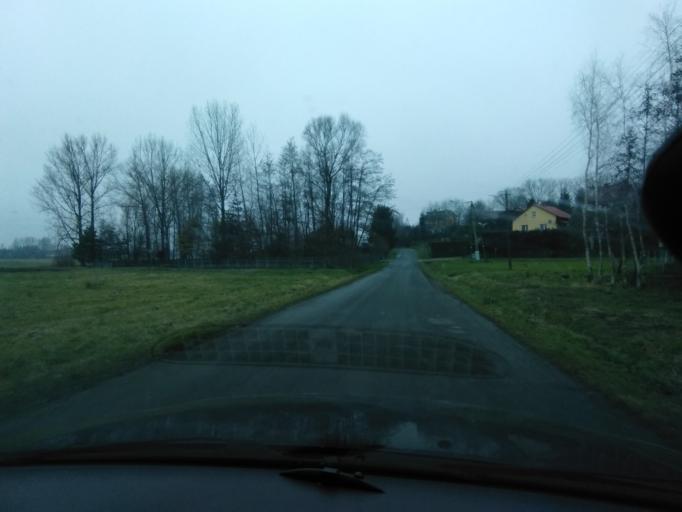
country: PL
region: Subcarpathian Voivodeship
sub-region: Powiat przeworski
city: Zarzecze
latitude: 49.9617
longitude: 22.5675
